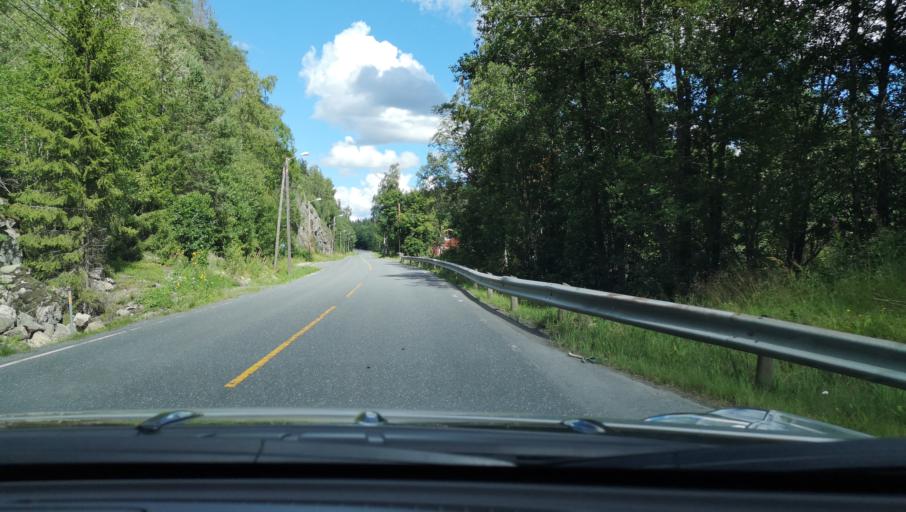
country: NO
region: Ostfold
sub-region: Hobol
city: Tomter
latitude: 59.6509
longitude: 10.9944
